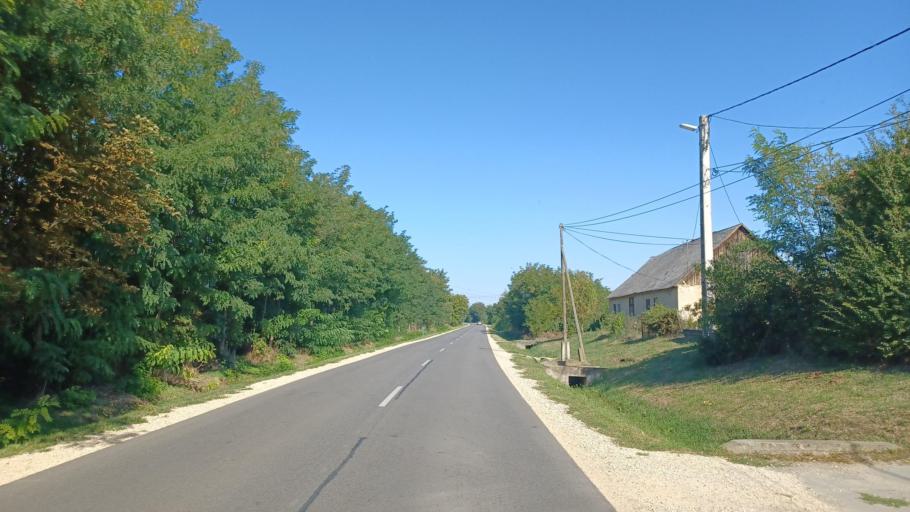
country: HU
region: Tolna
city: Nemetker
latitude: 46.6894
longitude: 18.7998
